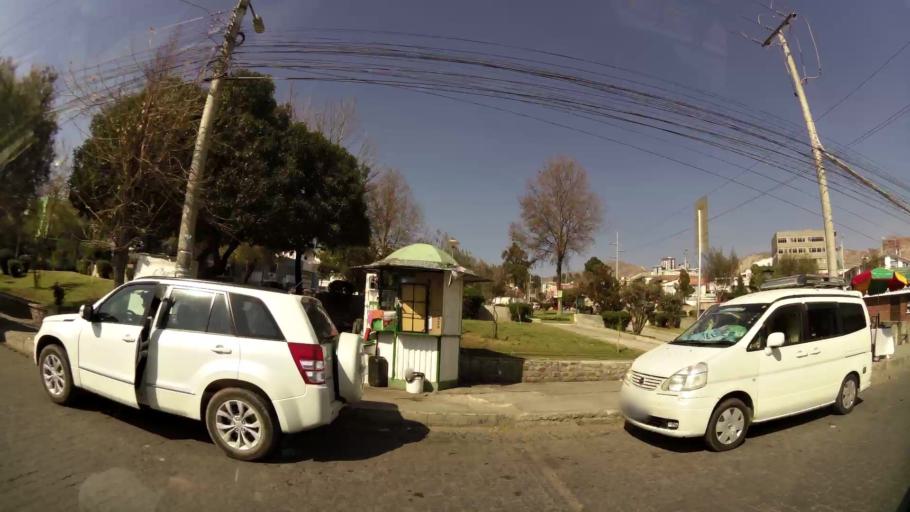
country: BO
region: La Paz
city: La Paz
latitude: -16.5357
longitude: -68.0755
